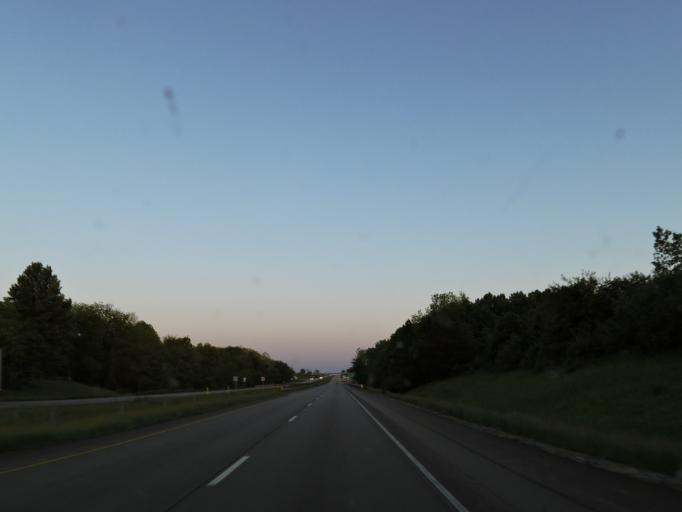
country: US
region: Indiana
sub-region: Montgomery County
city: Crawfordsville
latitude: 40.0528
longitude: -86.8191
